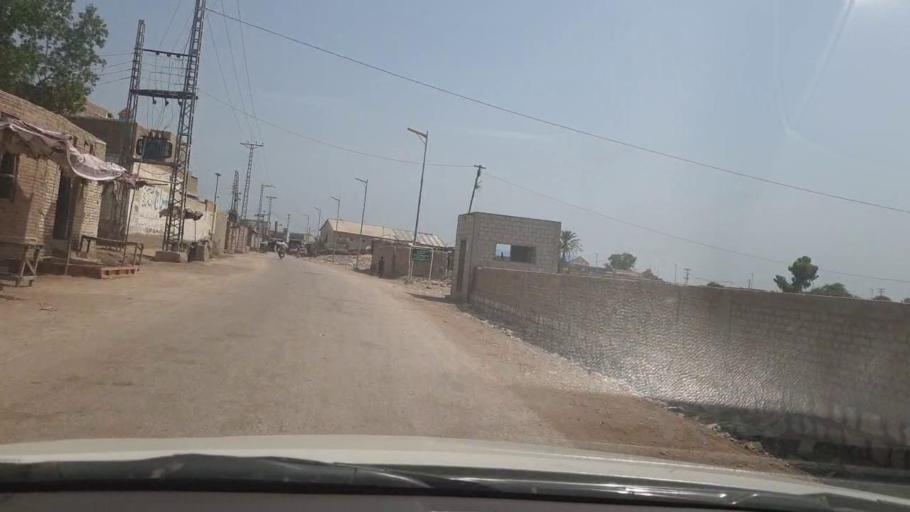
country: PK
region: Sindh
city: Garhi Yasin
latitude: 27.9050
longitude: 68.5069
